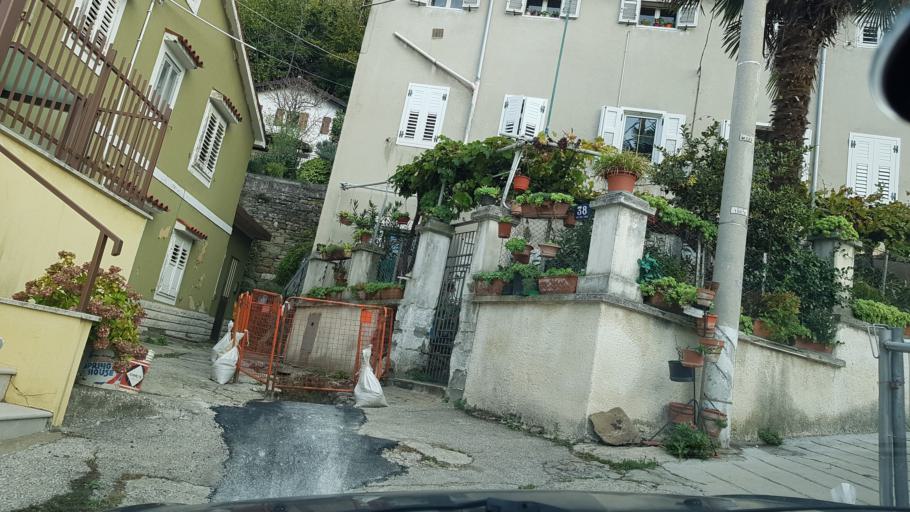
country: IT
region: Friuli Venezia Giulia
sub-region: Provincia di Trieste
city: Trieste
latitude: 45.6512
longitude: 13.8172
